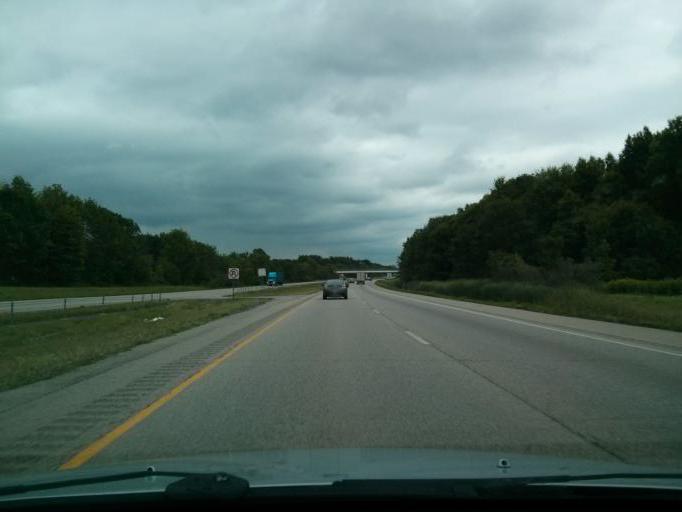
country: US
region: Ohio
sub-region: Mahoning County
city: Craig Beach
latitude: 41.1052
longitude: -81.0379
